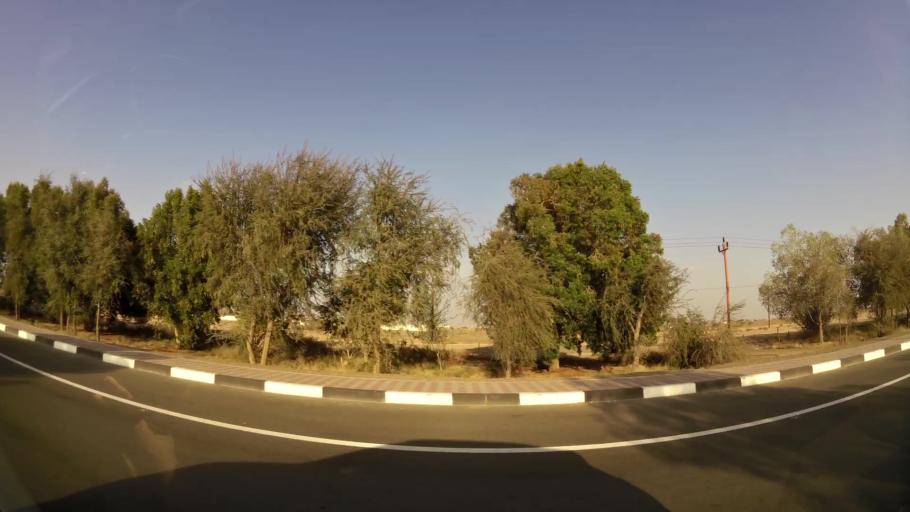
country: AE
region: Abu Dhabi
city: Al Ain
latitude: 24.1274
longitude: 55.8213
